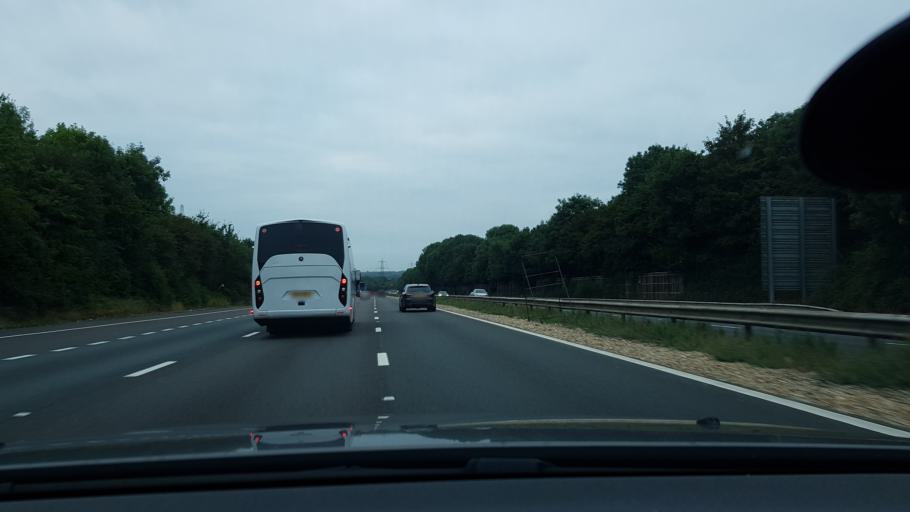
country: GB
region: England
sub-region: Hampshire
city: Eastleigh
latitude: 50.9913
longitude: -1.3602
